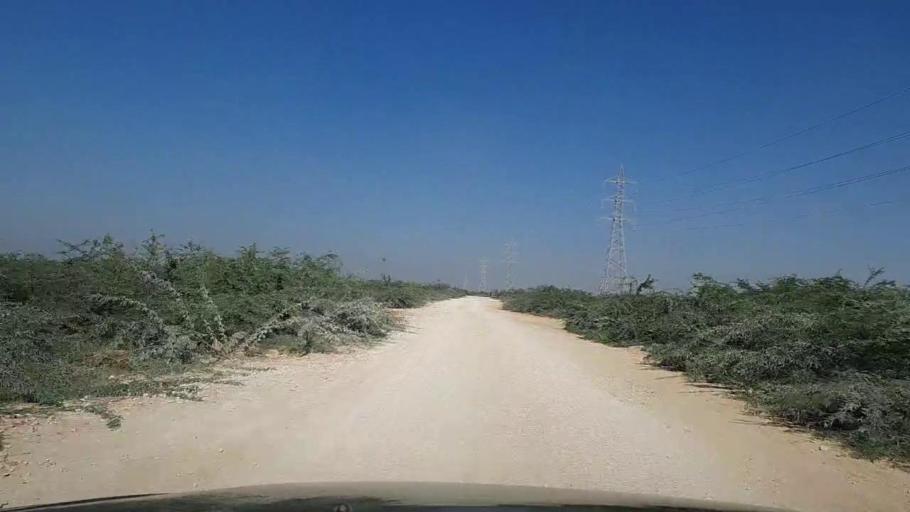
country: PK
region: Sindh
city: Thatta
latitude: 24.6263
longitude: 67.8344
